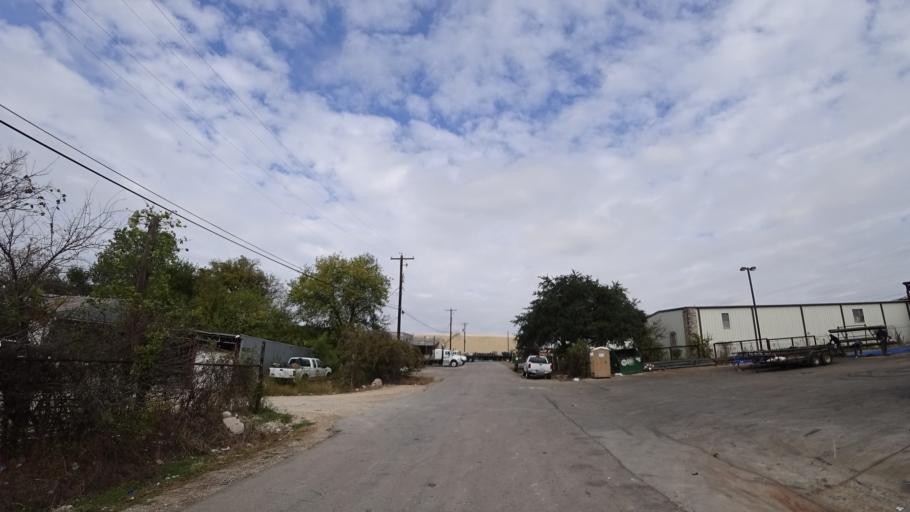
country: US
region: Texas
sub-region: Travis County
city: Wells Branch
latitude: 30.4322
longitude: -97.6840
